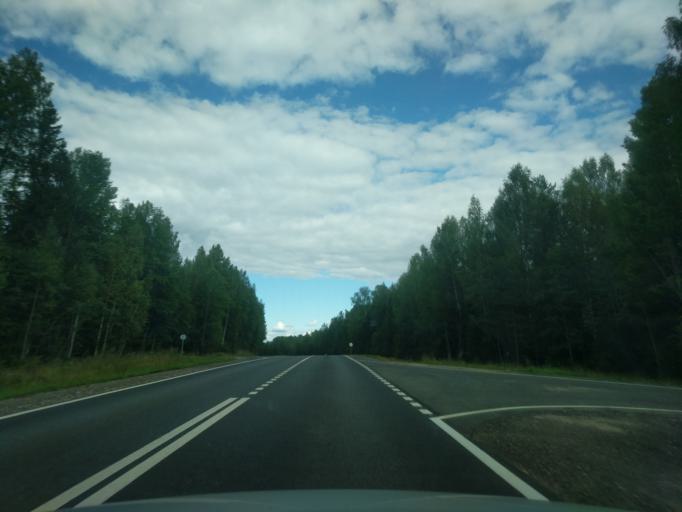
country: RU
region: Kostroma
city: Kadyy
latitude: 57.8419
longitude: 43.4431
